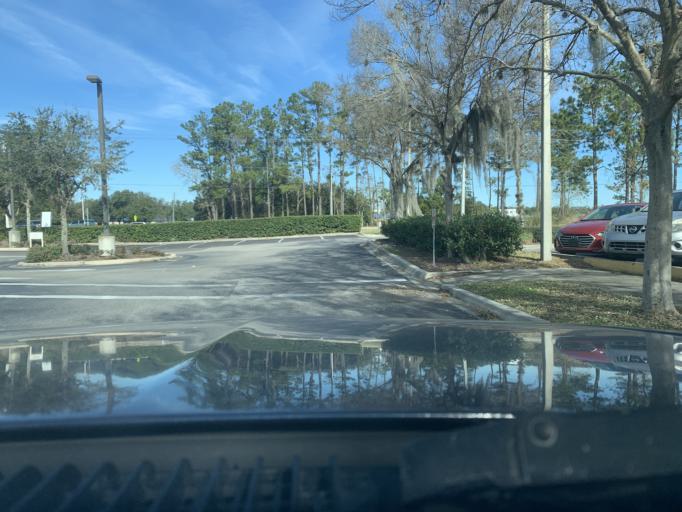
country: US
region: Florida
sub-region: Saint Johns County
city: Saint Augustine
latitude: 29.9625
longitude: -81.4907
